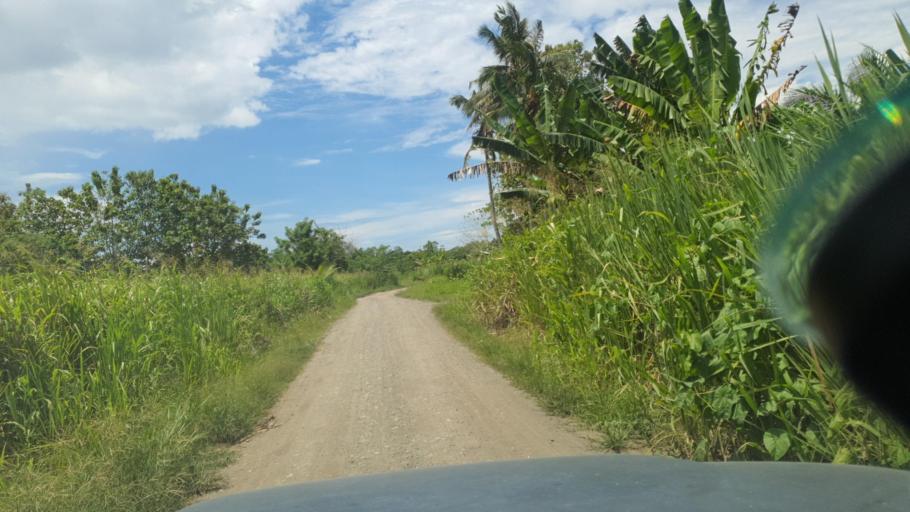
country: SB
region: Guadalcanal
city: Honiara
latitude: -9.4473
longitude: 160.1832
